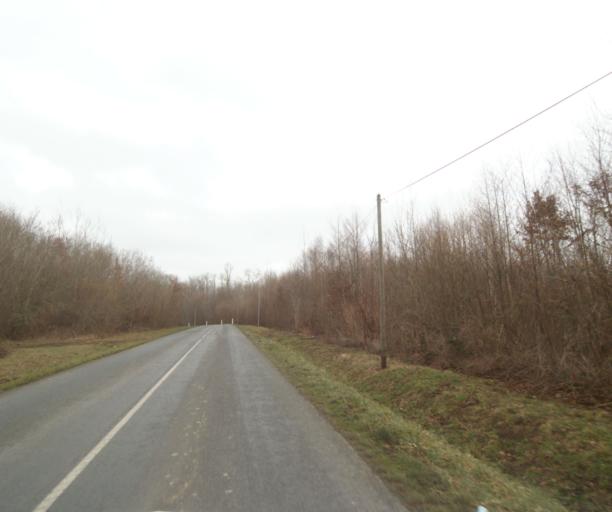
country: FR
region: Champagne-Ardenne
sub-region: Departement de la Haute-Marne
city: Villiers-en-Lieu
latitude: 48.6928
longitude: 4.8916
